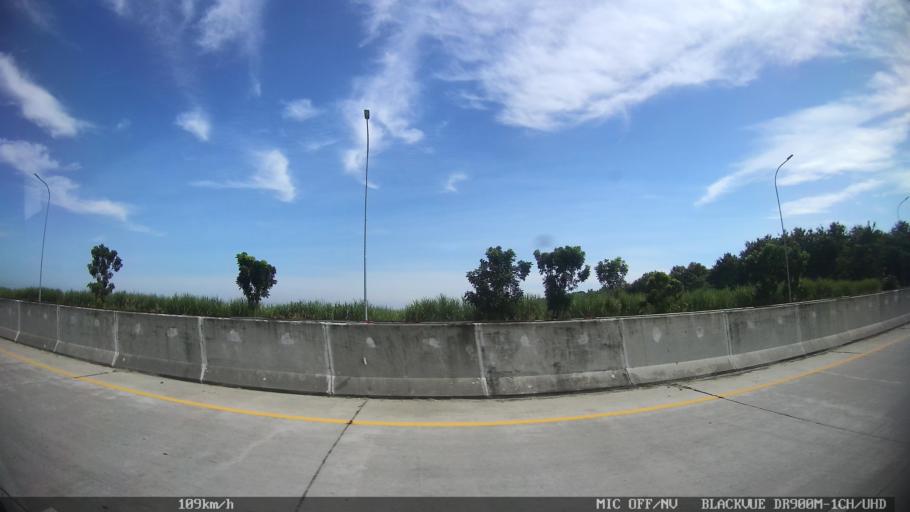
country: ID
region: North Sumatra
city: Sunggal
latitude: 3.6379
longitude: 98.6331
